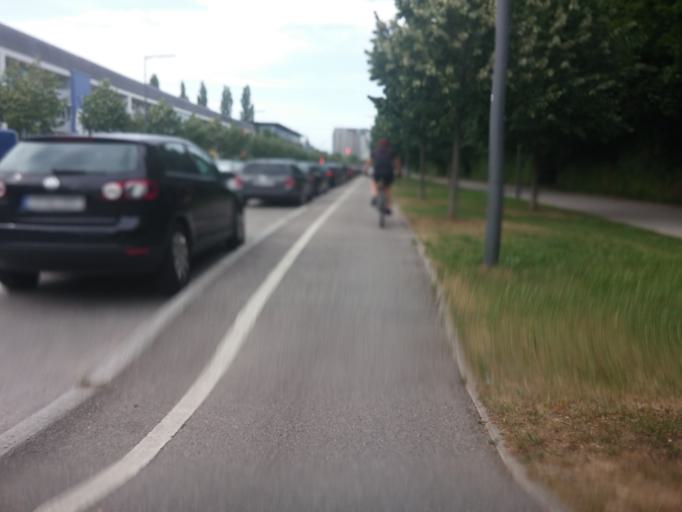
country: DE
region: Bavaria
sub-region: Upper Bavaria
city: Bogenhausen
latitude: 48.1440
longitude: 11.6157
